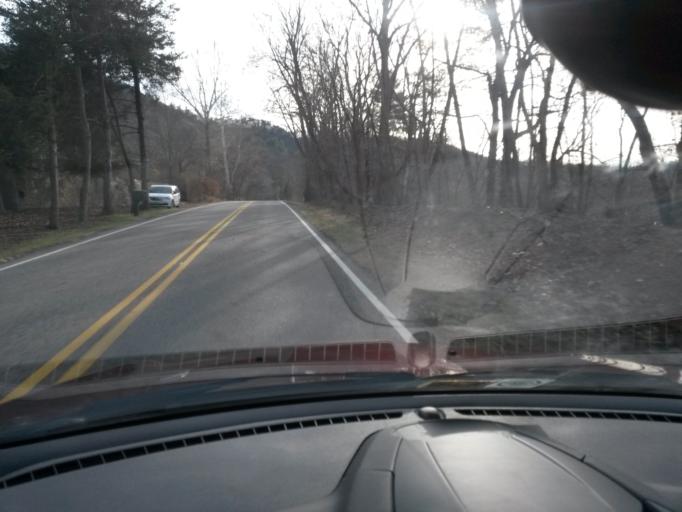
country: US
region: Virginia
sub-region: Alleghany County
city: Clifton Forge
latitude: 37.9136
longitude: -79.7264
